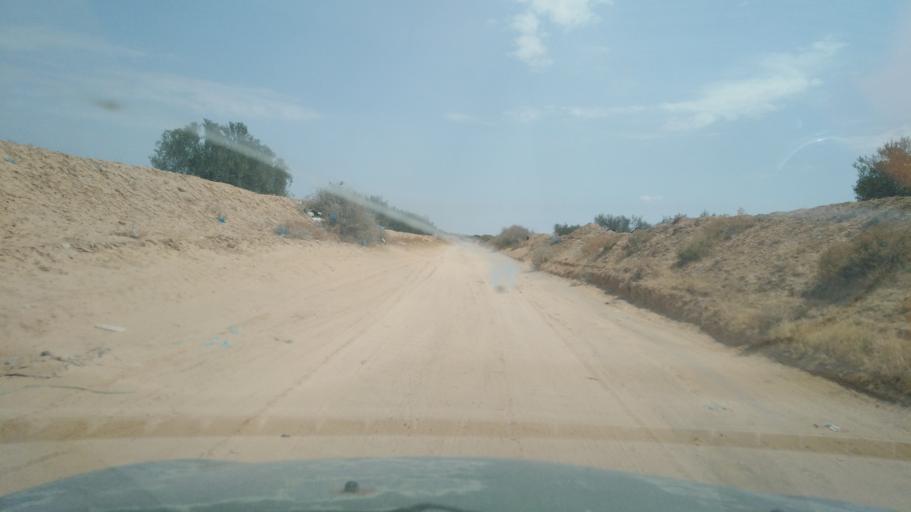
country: TN
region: Safaqis
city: Sfax
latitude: 34.7384
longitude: 10.5560
